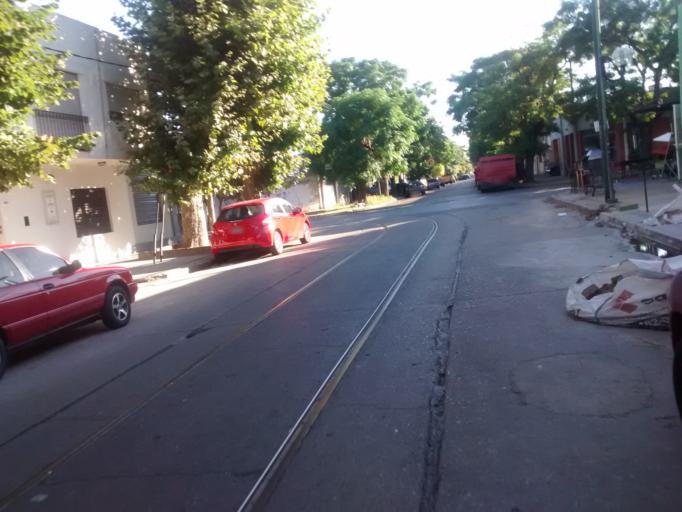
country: AR
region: Buenos Aires
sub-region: Partido de La Plata
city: La Plata
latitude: -34.9285
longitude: -57.9273
